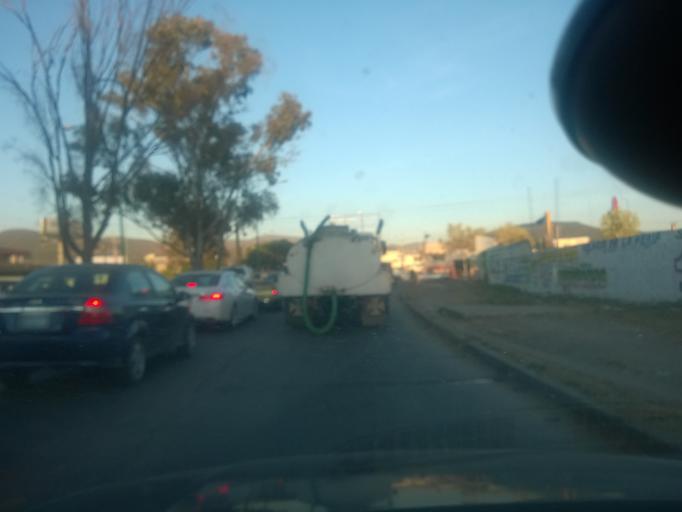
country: MX
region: Guanajuato
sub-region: Leon
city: Medina
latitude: 21.1454
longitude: -101.6346
